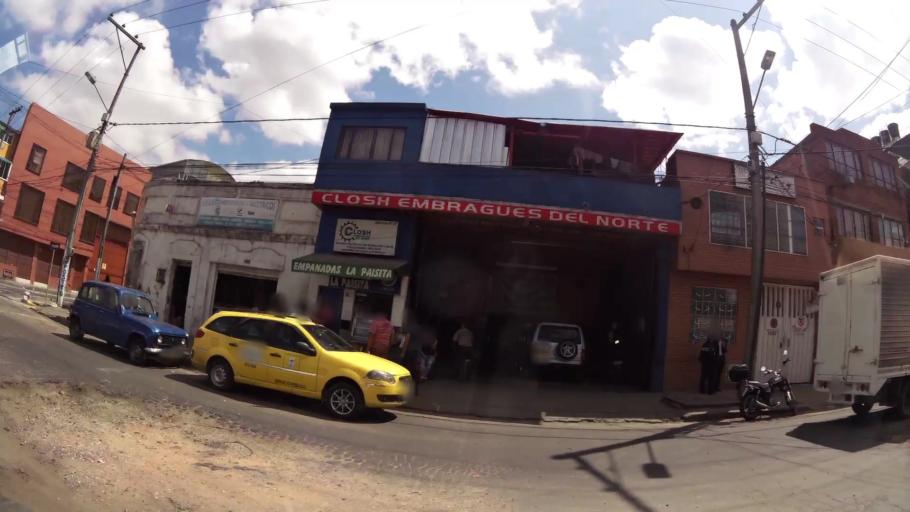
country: CO
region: Bogota D.C.
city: Bogota
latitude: 4.6167
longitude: -74.0814
